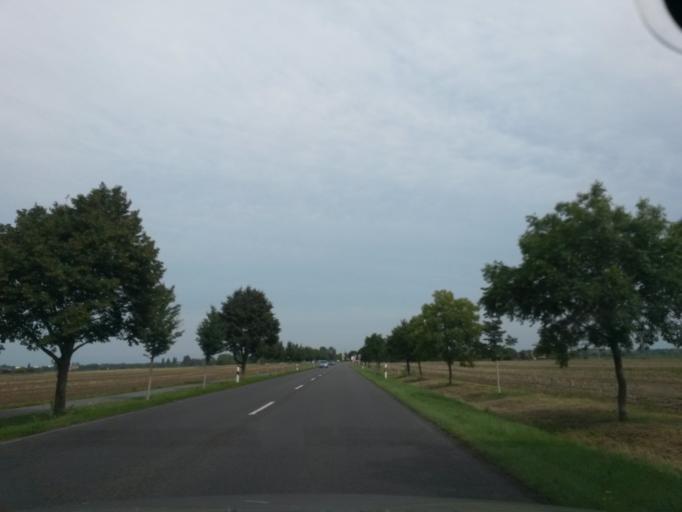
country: DE
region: Brandenburg
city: Meyenburg
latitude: 53.0427
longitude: 14.2610
